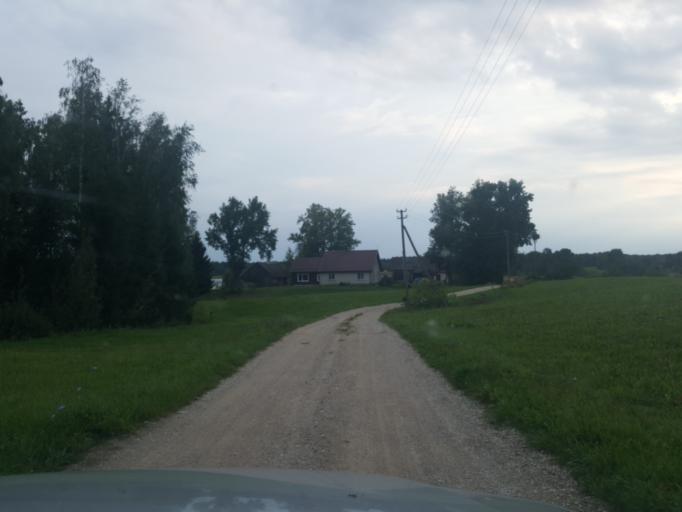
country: LT
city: Veisiejai
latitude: 54.1203
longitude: 23.5937
